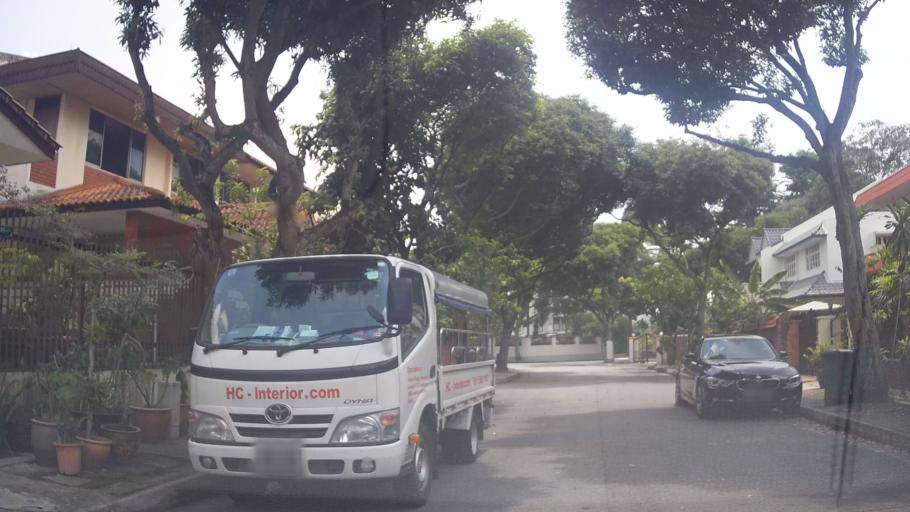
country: SG
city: Singapore
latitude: 1.3599
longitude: 103.8690
